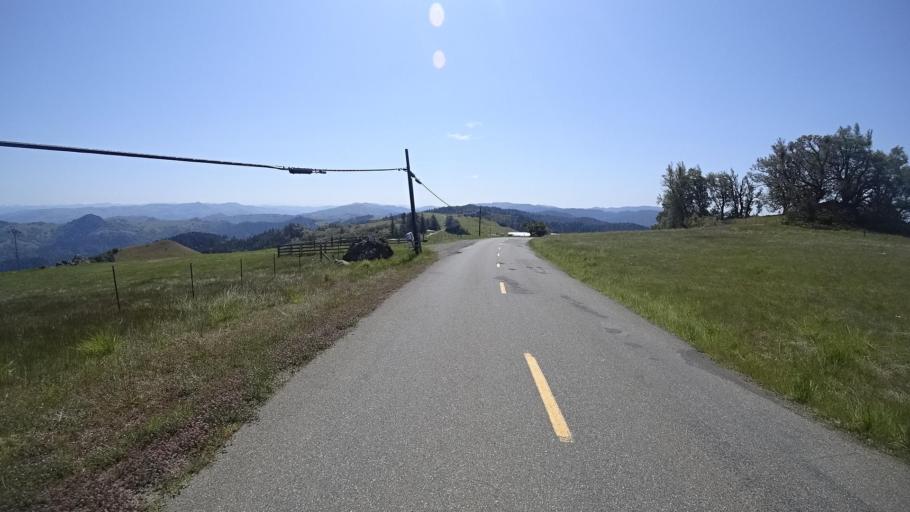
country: US
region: California
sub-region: Humboldt County
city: Redway
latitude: 40.0908
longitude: -123.6774
